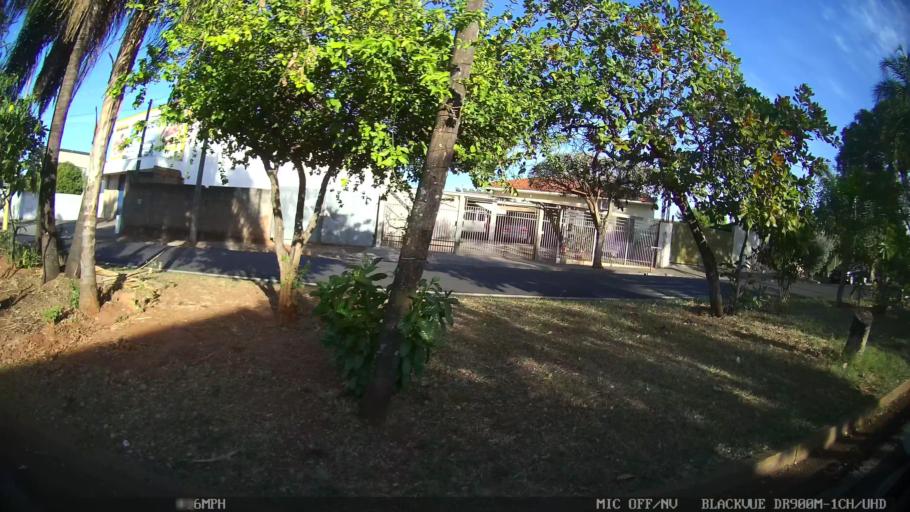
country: BR
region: Sao Paulo
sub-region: Sao Jose Do Rio Preto
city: Sao Jose do Rio Preto
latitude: -20.8308
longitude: -49.3691
